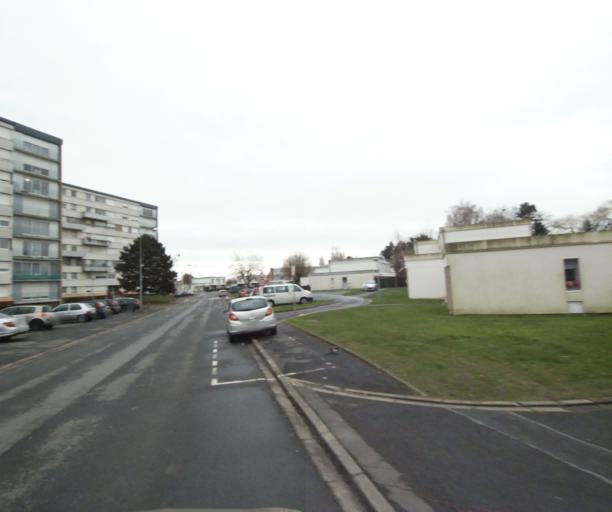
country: FR
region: Nord-Pas-de-Calais
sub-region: Departement du Nord
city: La Sentinelle
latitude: 50.3527
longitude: 3.4845
